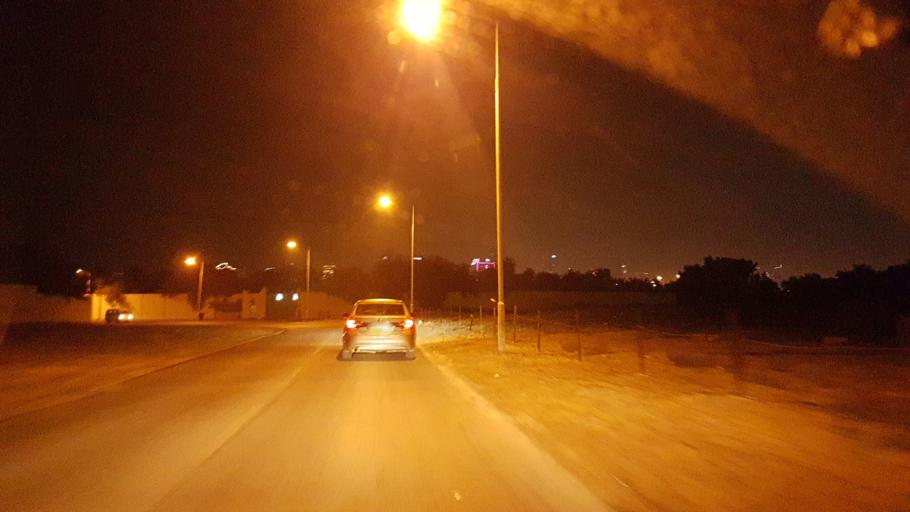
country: BH
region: Manama
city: Jidd Hafs
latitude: 26.2286
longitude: 50.5228
